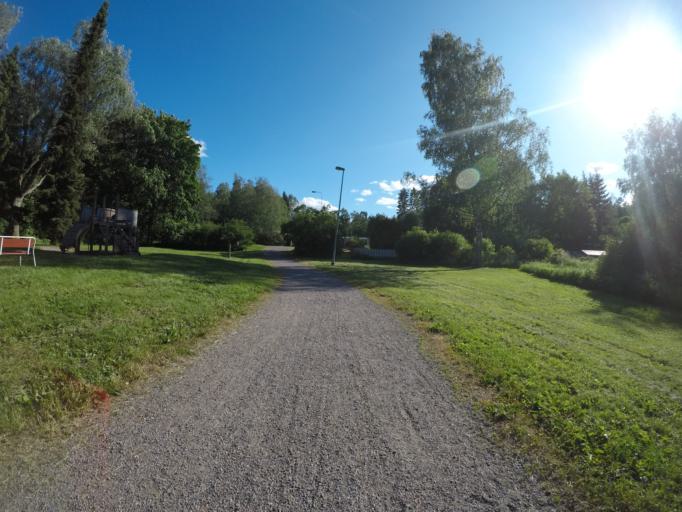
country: FI
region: Haeme
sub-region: Haemeenlinna
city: Haemeenlinna
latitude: 61.0153
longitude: 24.4956
